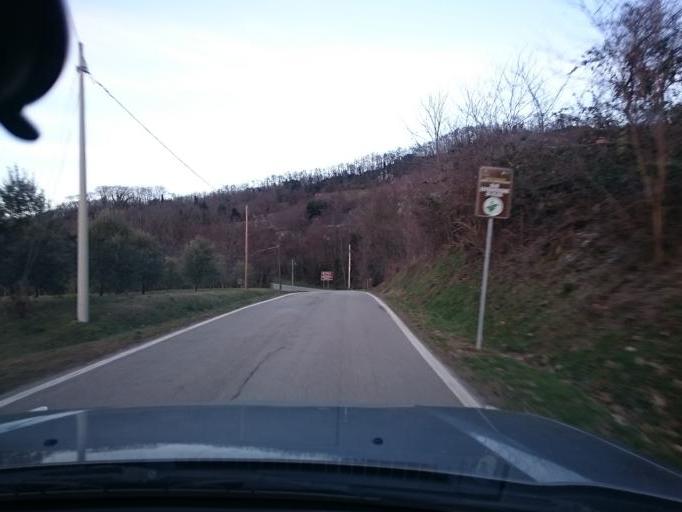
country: IT
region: Veneto
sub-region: Provincia di Padova
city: Fontanafredda
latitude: 45.3210
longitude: 11.6801
